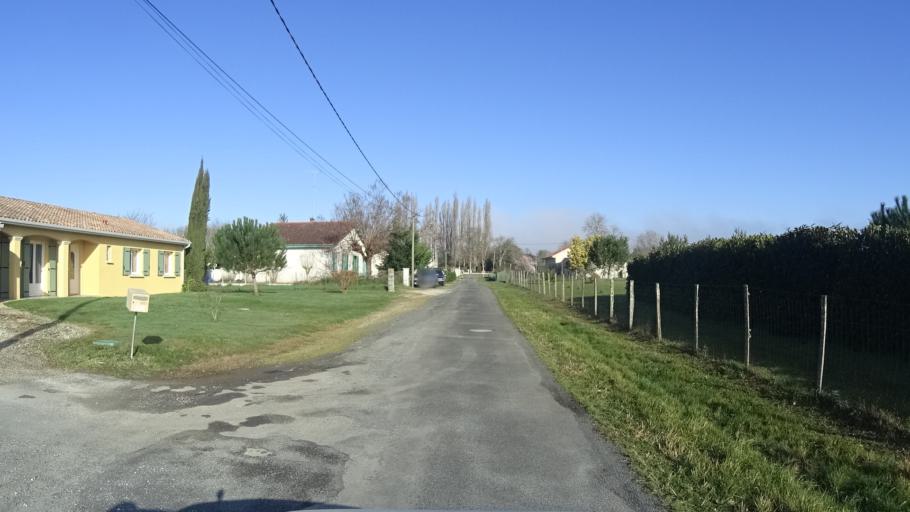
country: FR
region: Poitou-Charentes
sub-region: Departement de la Charente-Maritime
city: Saint-Aigulin
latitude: 45.1532
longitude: -0.0038
